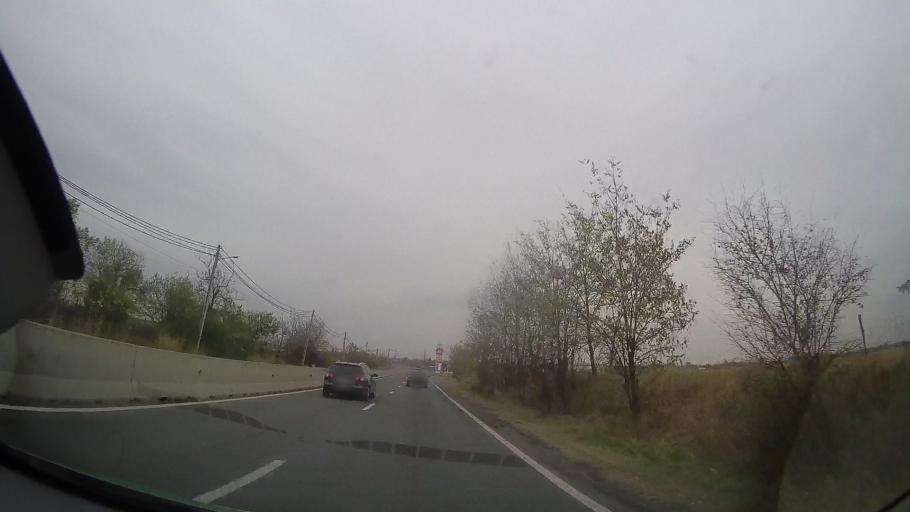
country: RO
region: Prahova
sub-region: Comuna Albesti-Paleologu
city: Albesti-Paleologu
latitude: 44.9541
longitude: 26.2164
